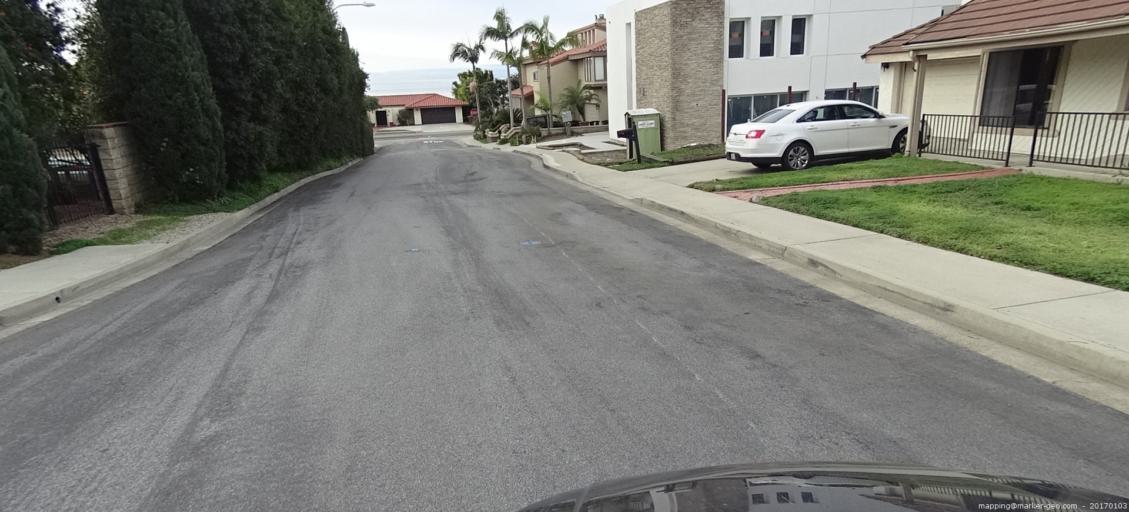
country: US
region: California
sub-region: Orange County
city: Dana Point
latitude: 33.4522
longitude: -117.6575
